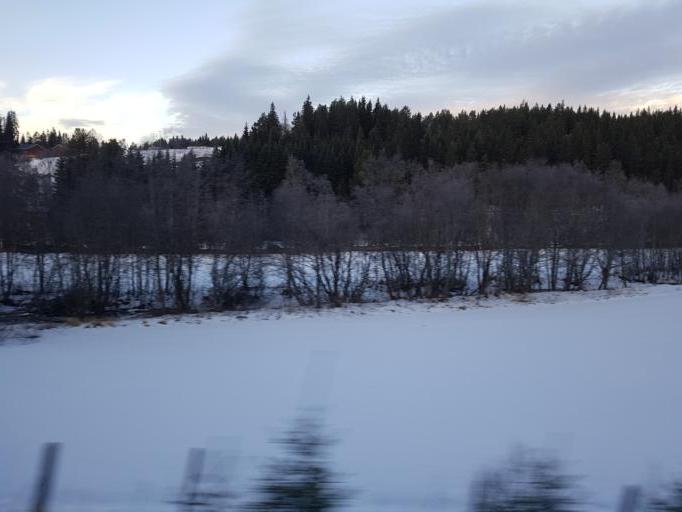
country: NO
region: Sor-Trondelag
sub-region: Rennebu
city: Berkak
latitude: 62.8751
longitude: 10.0720
